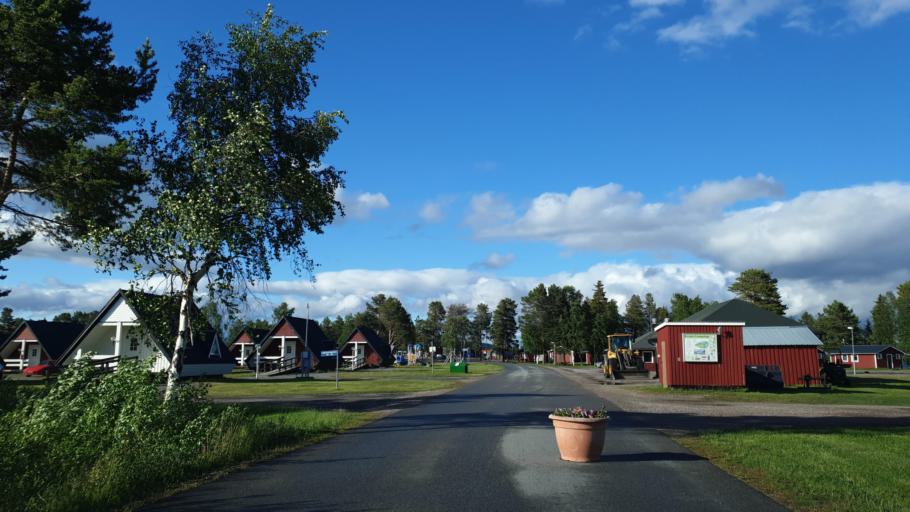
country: SE
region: Norrbotten
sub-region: Arjeplogs Kommun
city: Arjeplog
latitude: 66.0506
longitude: 17.8631
